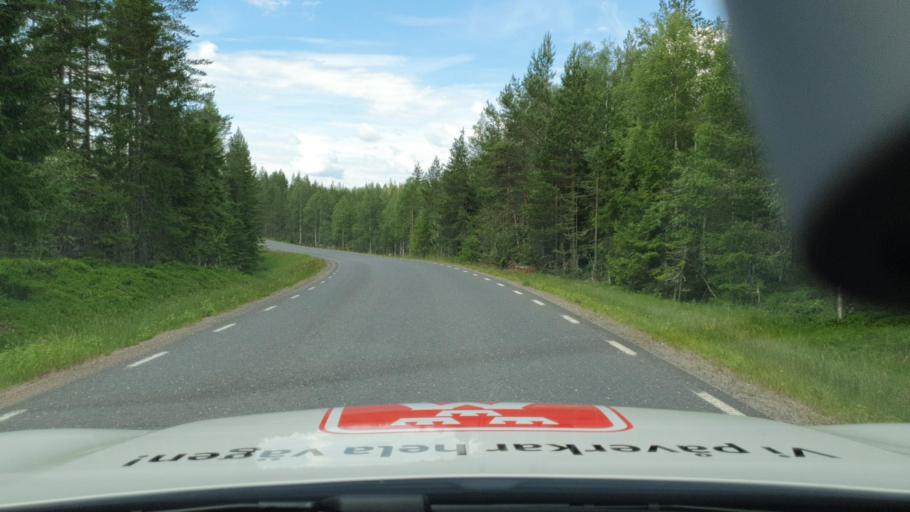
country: SE
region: Vaermland
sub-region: Torsby Kommun
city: Torsby
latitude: 60.5353
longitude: 12.8129
